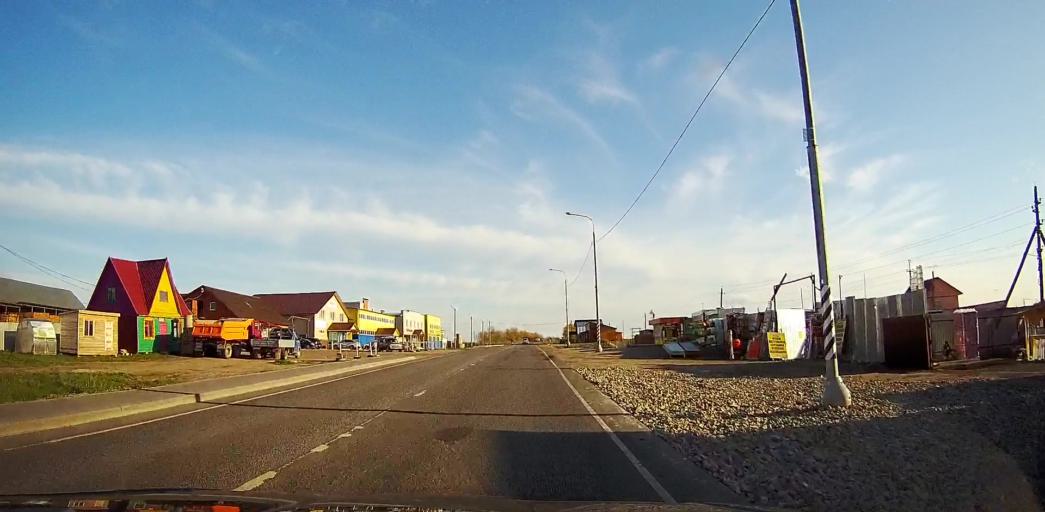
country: RU
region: Moskovskaya
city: Bronnitsy
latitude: 55.3260
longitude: 38.2193
